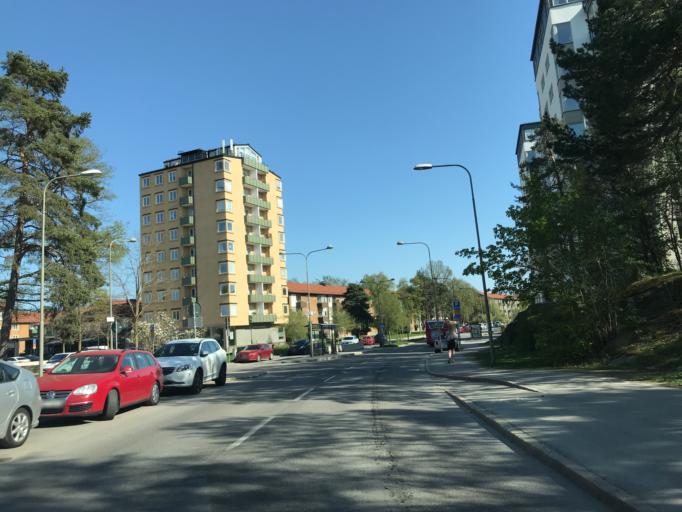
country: SE
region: Stockholm
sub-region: Stockholms Kommun
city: Arsta
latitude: 59.2872
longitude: 18.0085
